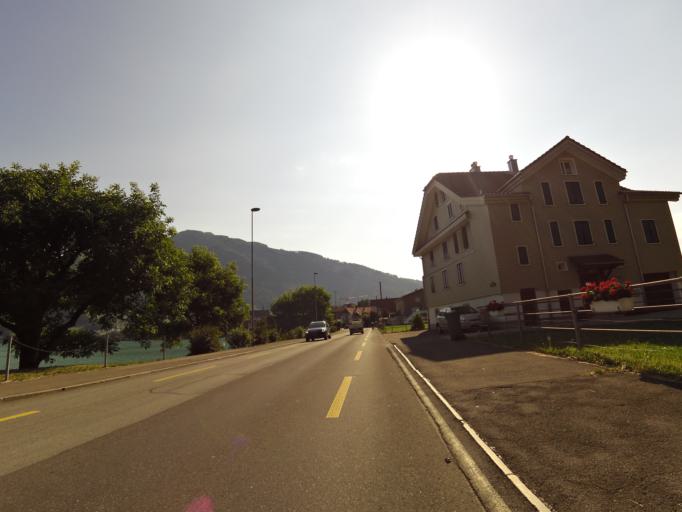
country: CH
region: Schwyz
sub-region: Bezirk Schwyz
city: Arth
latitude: 47.0613
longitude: 8.5172
